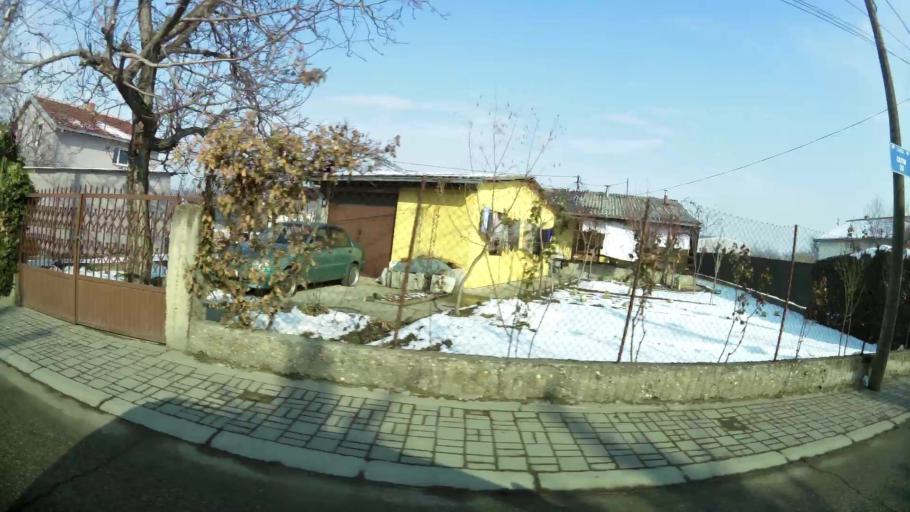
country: MK
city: Krushopek
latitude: 42.0152
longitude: 21.3794
